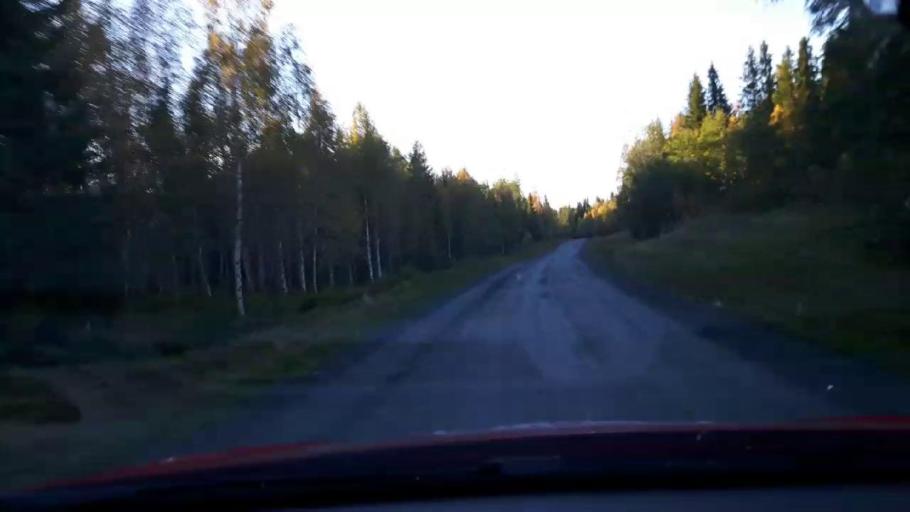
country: SE
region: Jaemtland
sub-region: Krokoms Kommun
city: Krokom
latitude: 63.4473
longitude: 14.5771
